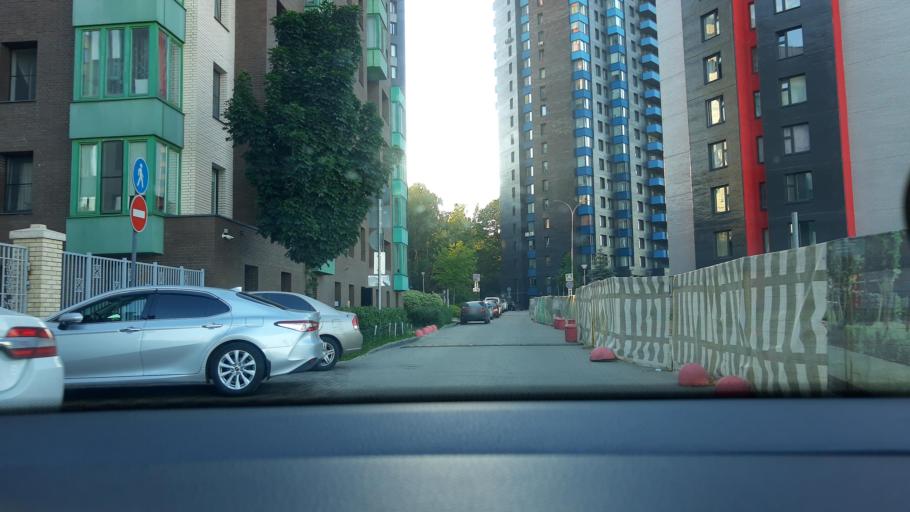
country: RU
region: Moskovskaya
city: Firsanovka
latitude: 55.9430
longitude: 37.2626
